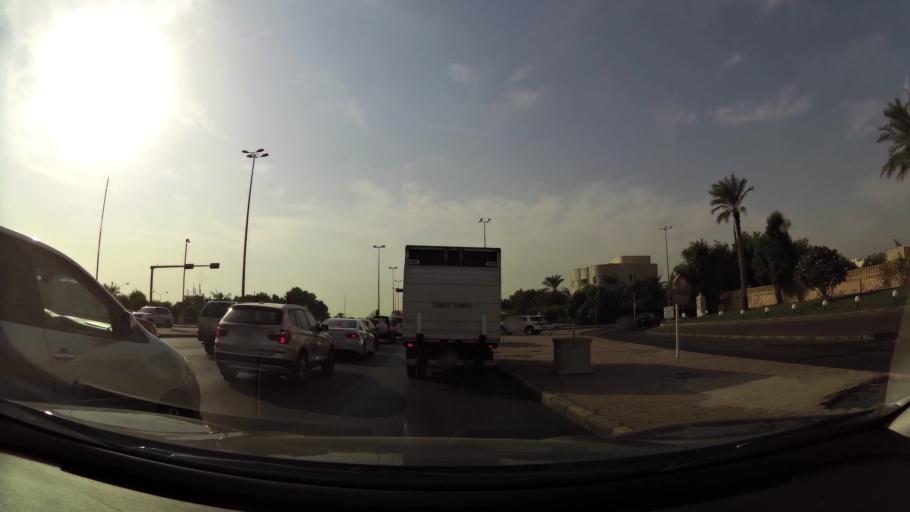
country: KW
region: Muhafazat Hawalli
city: Salwa
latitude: 29.2806
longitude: 48.0876
